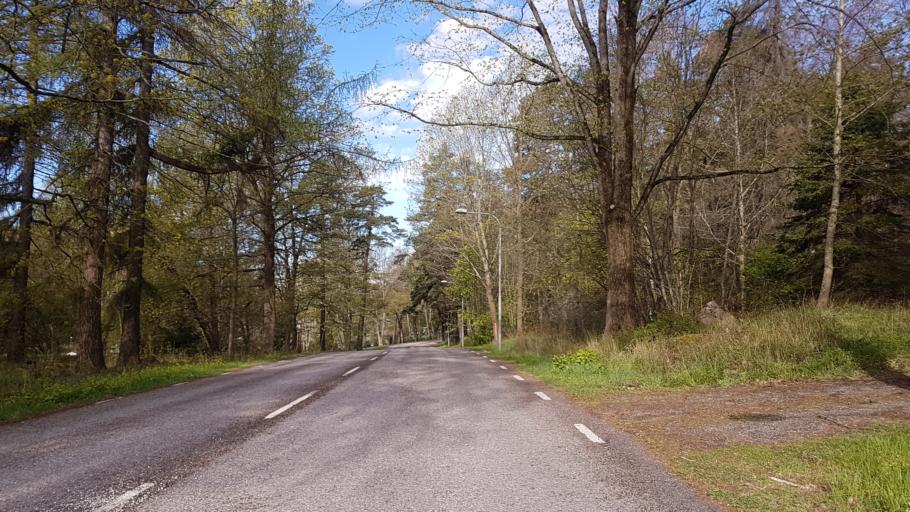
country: SE
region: Stockholm
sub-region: Stockholms Kommun
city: Stockholm
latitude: 59.3562
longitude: 18.0683
